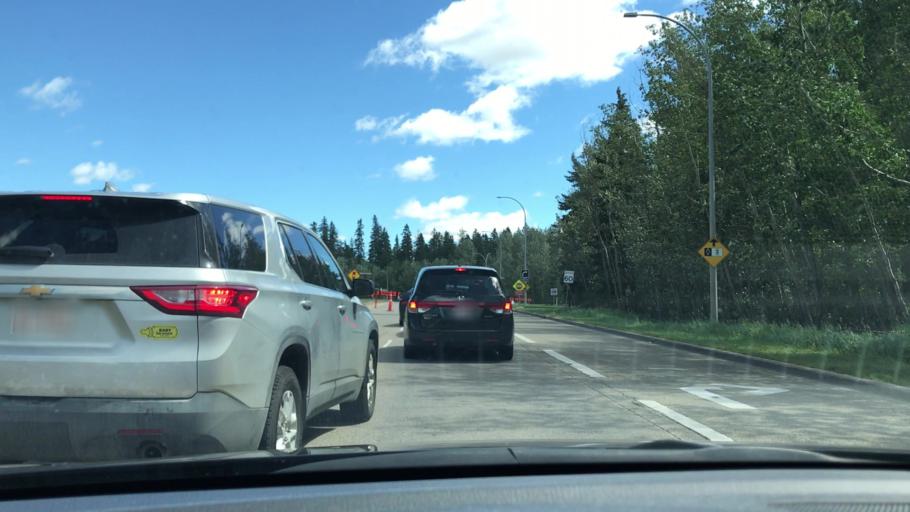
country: CA
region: Alberta
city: Edmonton
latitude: 53.5048
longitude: -113.5414
